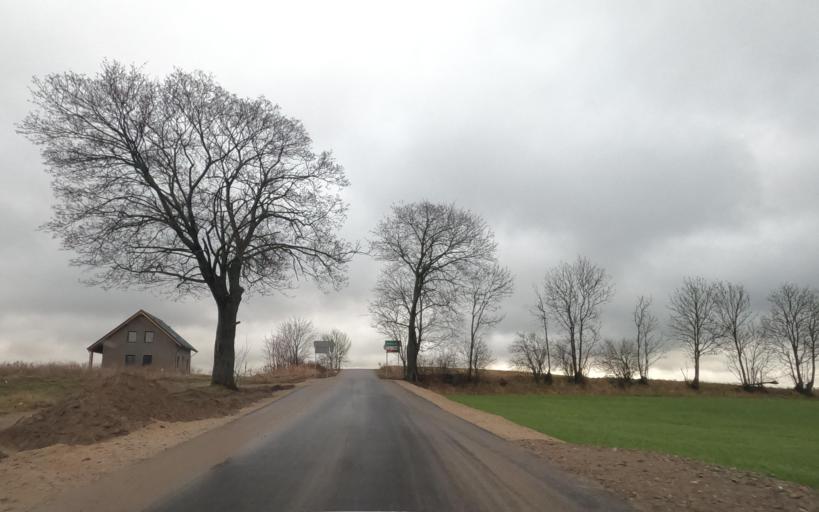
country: PL
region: West Pomeranian Voivodeship
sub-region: Powiat szczecinecki
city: Szczecinek
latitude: 53.7106
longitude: 16.7347
